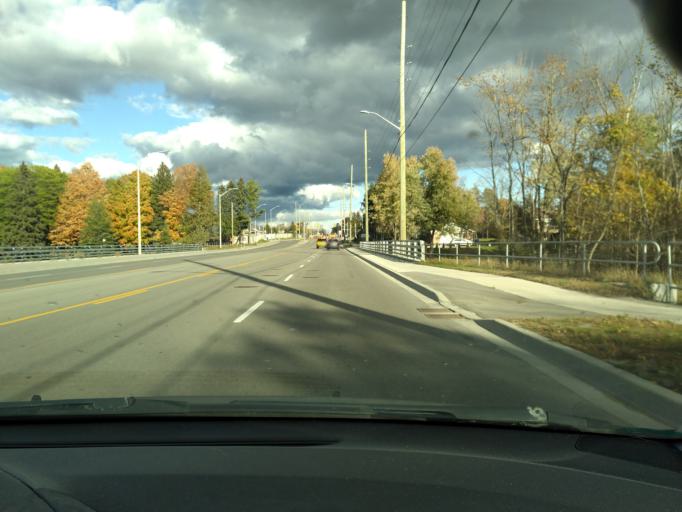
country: CA
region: Ontario
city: Innisfil
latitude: 44.3421
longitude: -79.6554
